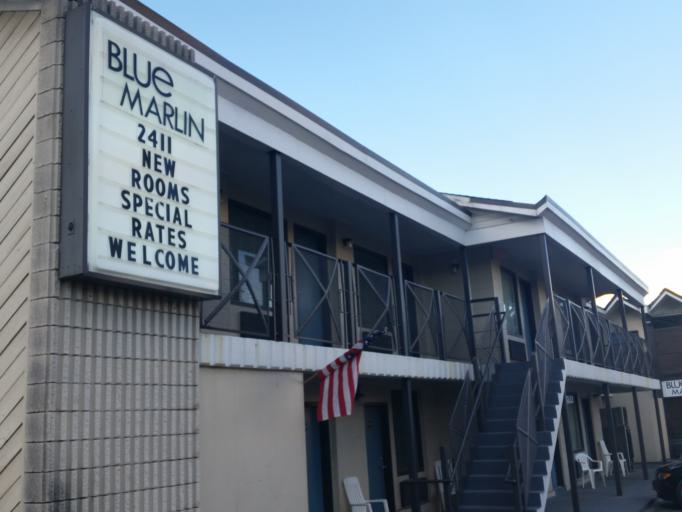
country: US
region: Virginia
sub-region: City of Virginia Beach
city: Virginia Beach
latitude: 36.8528
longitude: -75.9774
